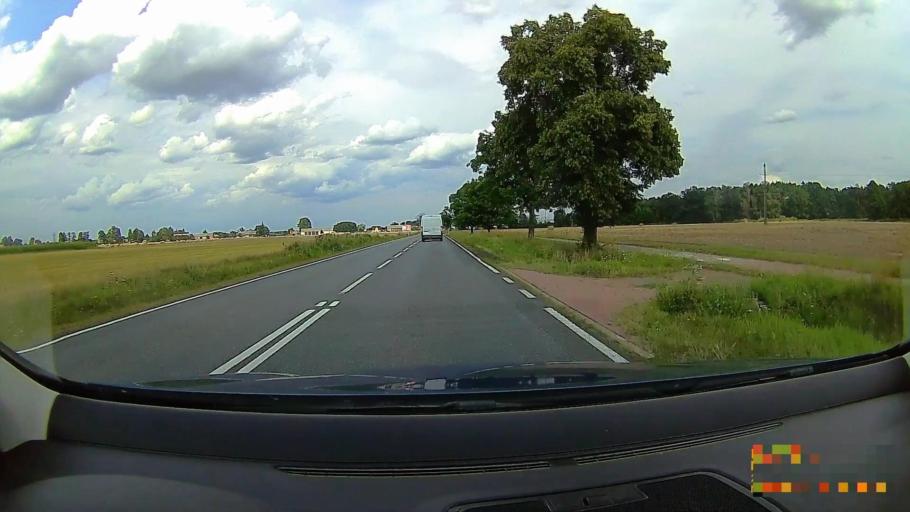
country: PL
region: Greater Poland Voivodeship
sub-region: Powiat koninski
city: Rychwal
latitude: 52.0894
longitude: 18.1643
